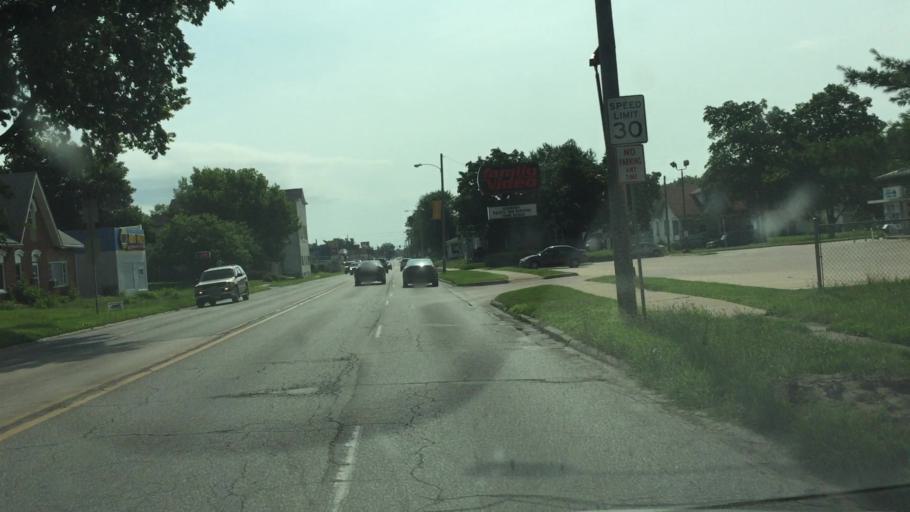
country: US
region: Iowa
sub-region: Lee County
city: Fort Madison
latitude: 40.6302
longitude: -91.3293
